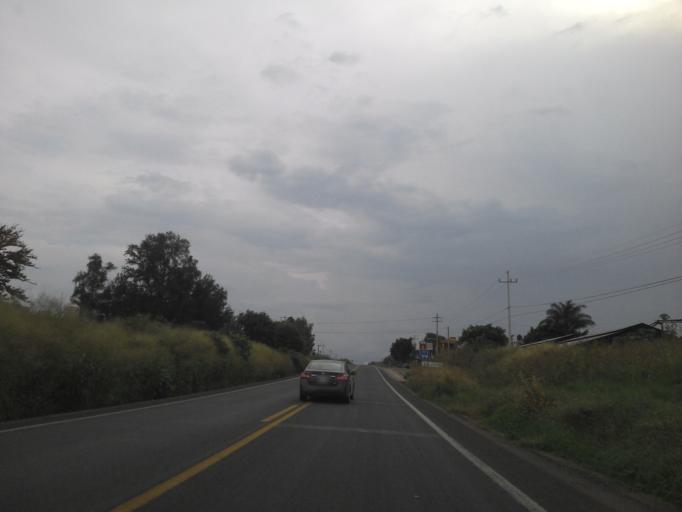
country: MX
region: Jalisco
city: Zapotlanejo
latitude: 20.6883
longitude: -102.9906
